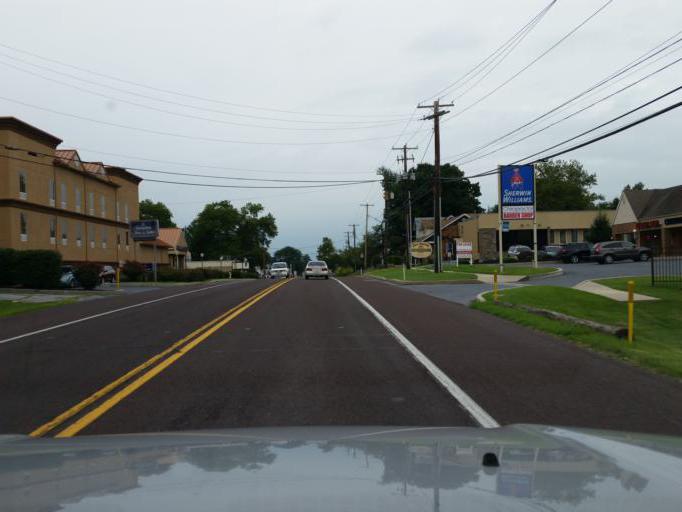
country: US
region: Pennsylvania
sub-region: Dauphin County
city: Palmdale
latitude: 40.2918
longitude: -76.6338
